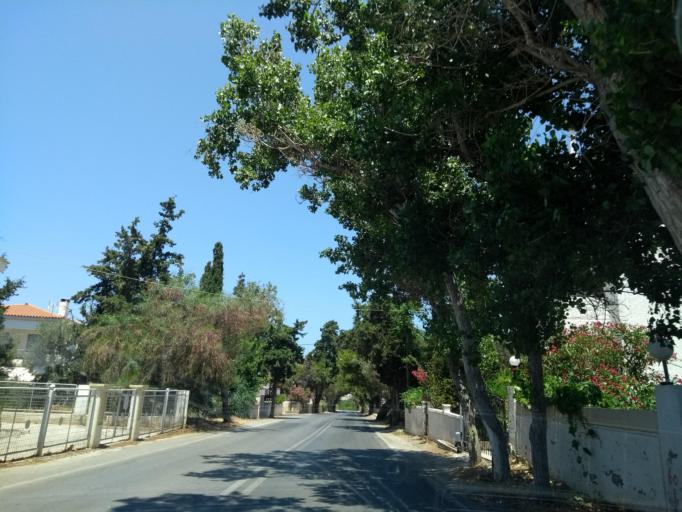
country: GR
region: Crete
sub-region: Nomos Chanias
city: Pithari
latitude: 35.5482
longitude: 24.0834
